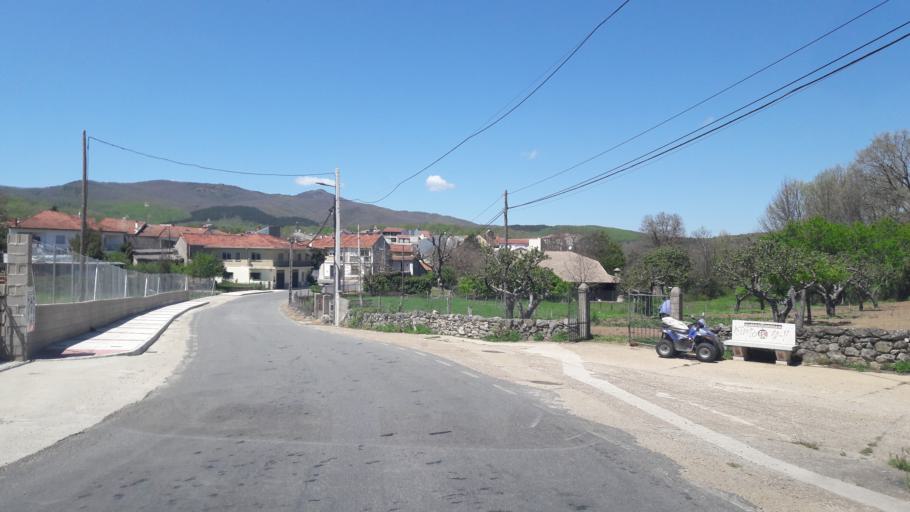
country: ES
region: Castille and Leon
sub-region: Provincia de Salamanca
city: Linares de Riofrio
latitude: 40.5835
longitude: -5.9166
